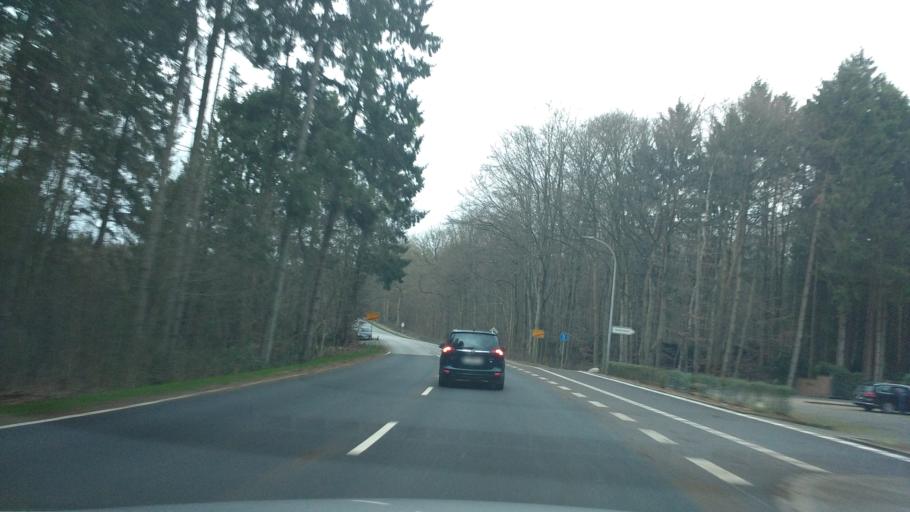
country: DE
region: Schleswig-Holstein
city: Itzehoe
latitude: 53.9343
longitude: 9.5386
